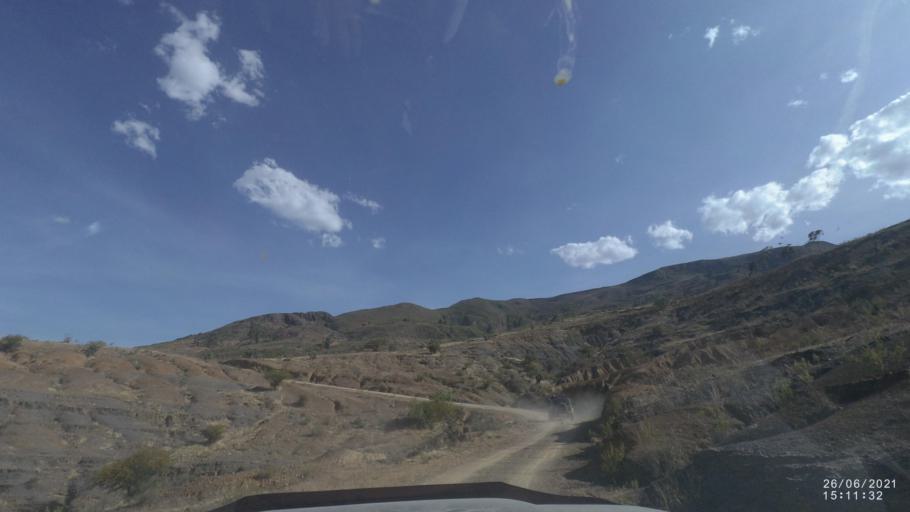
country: BO
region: Cochabamba
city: Mizque
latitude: -17.9563
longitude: -65.6427
